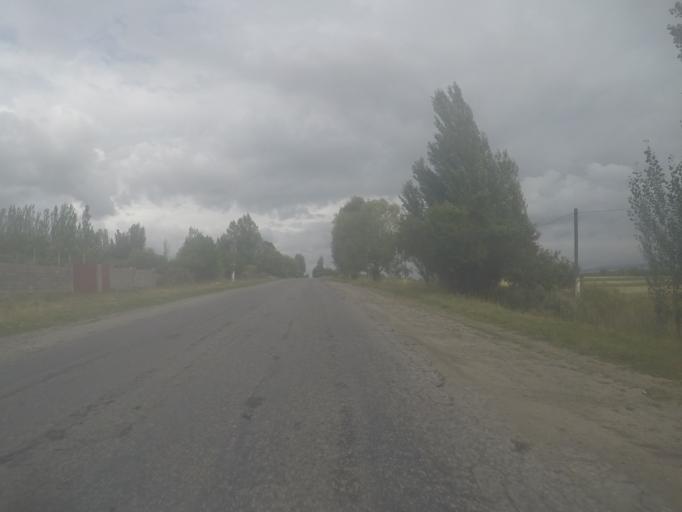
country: KG
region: Ysyk-Koel
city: Tyup
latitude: 42.7475
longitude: 78.0952
